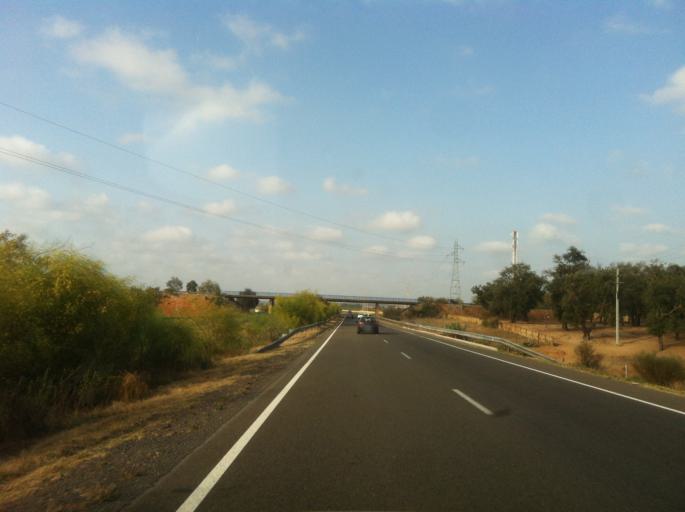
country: MA
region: Gharb-Chrarda-Beni Hssen
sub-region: Kenitra Province
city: Kenitra
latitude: 34.2299
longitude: -6.5734
